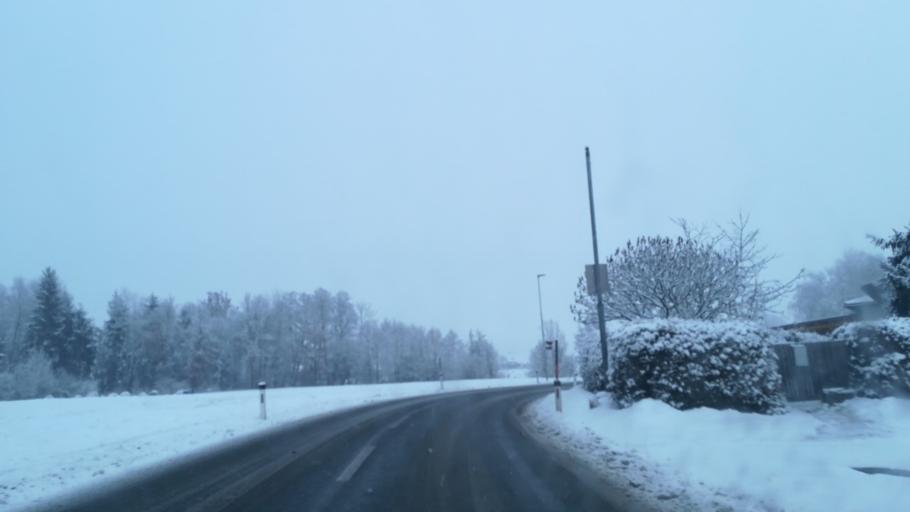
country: AT
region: Styria
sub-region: Politischer Bezirk Murtal
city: Spielberg bei Knittelfeld
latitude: 47.2169
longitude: 14.7939
